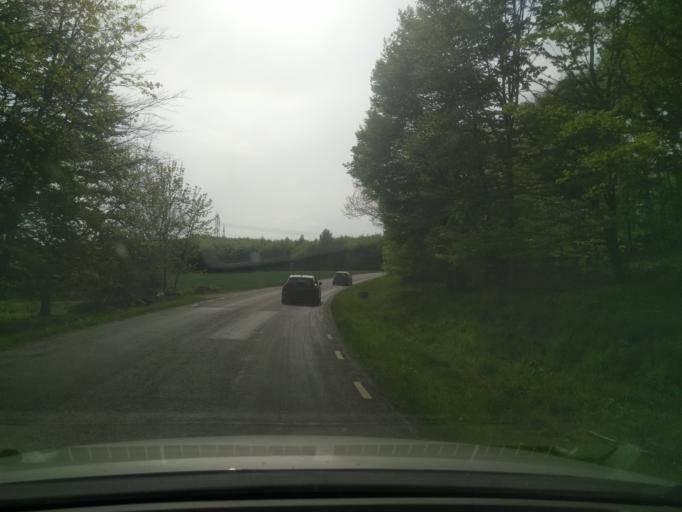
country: SE
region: Skane
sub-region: Svedala Kommun
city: Svedala
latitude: 55.5447
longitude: 13.1805
